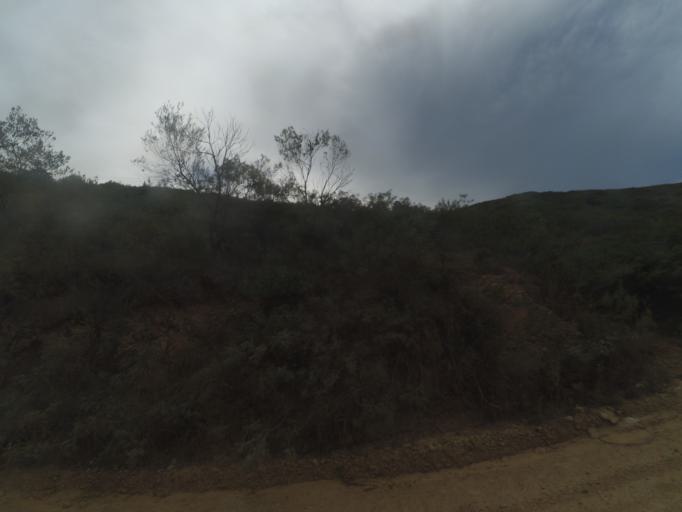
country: BO
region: Chuquisaca
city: Padilla
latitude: -19.3476
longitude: -64.2836
